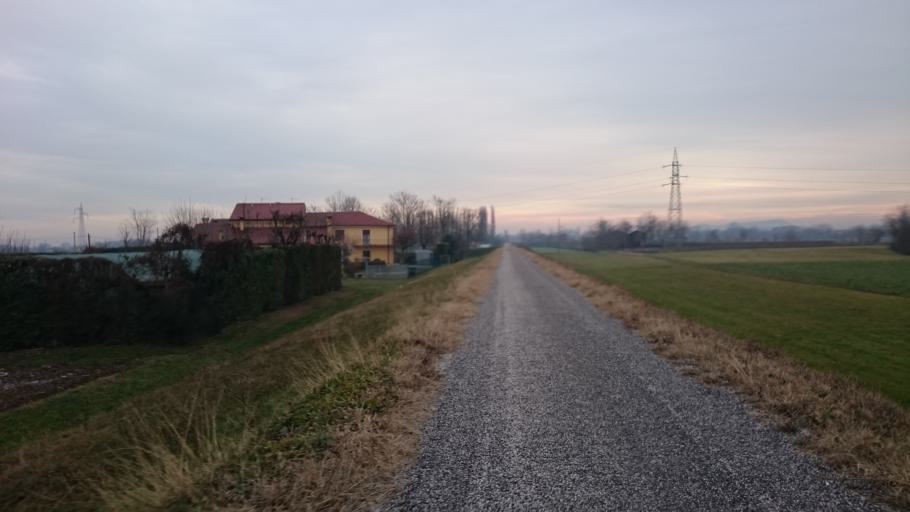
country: IT
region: Veneto
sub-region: Provincia di Vicenza
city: Montegaldella
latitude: 45.4360
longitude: 11.6825
